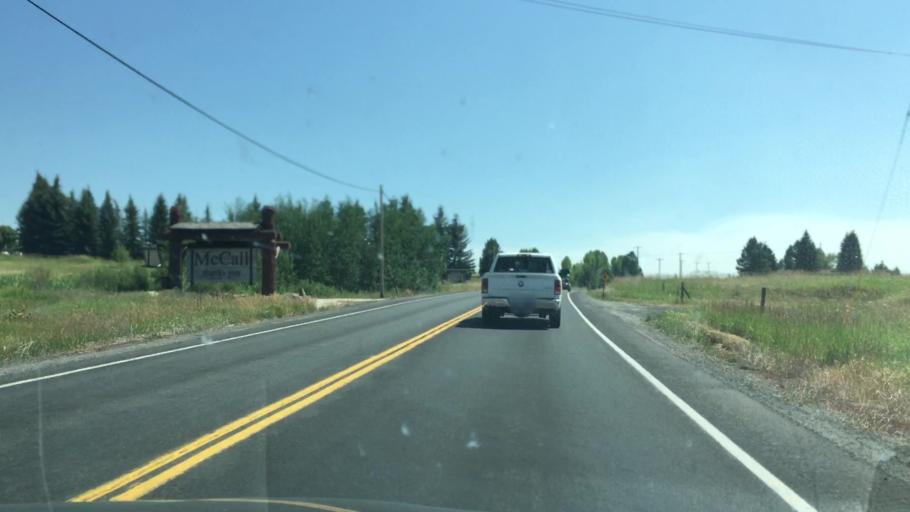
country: US
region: Idaho
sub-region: Valley County
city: McCall
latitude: 44.8861
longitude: -116.0915
